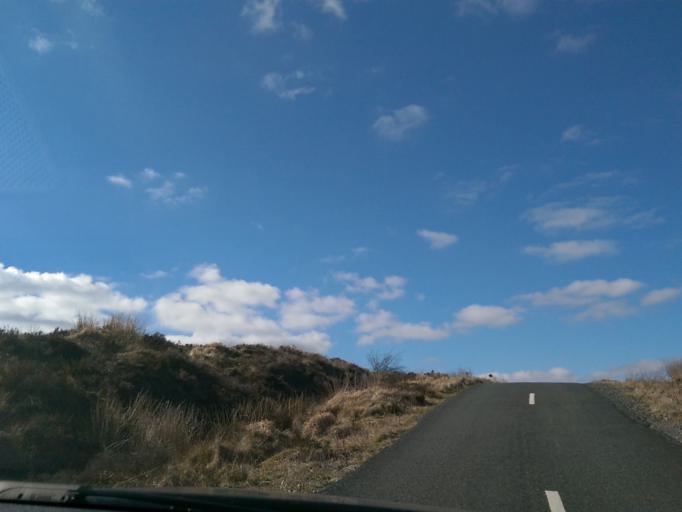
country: IE
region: Leinster
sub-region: Laois
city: Mountrath
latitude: 53.0770
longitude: -7.5924
